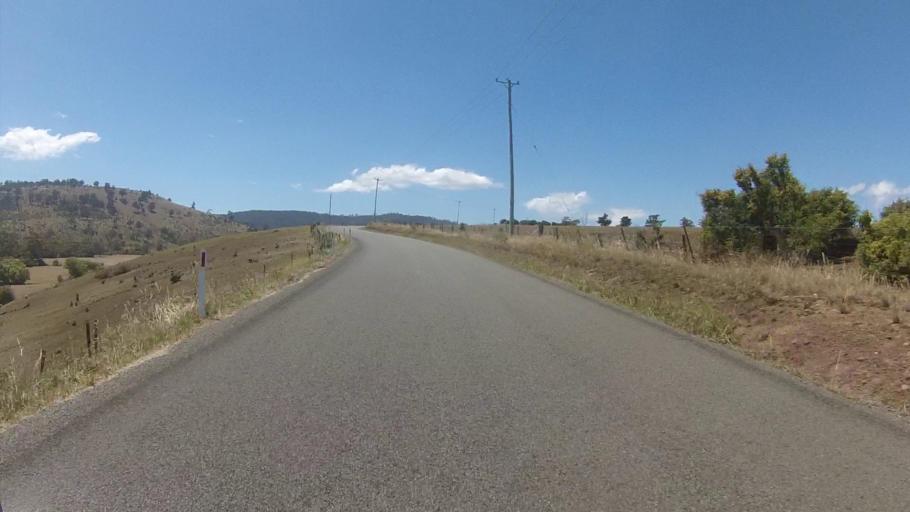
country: AU
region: Tasmania
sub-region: Sorell
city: Sorell
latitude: -42.7699
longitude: 147.5953
